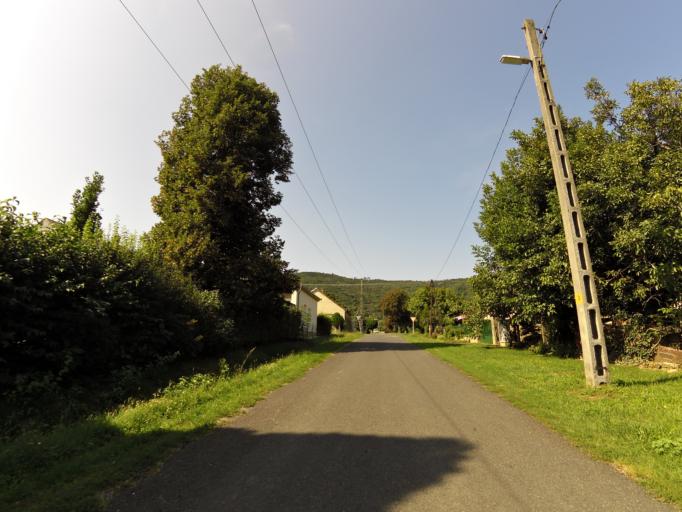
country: HU
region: Zala
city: Vonyarcvashegy
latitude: 46.8017
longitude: 17.3812
